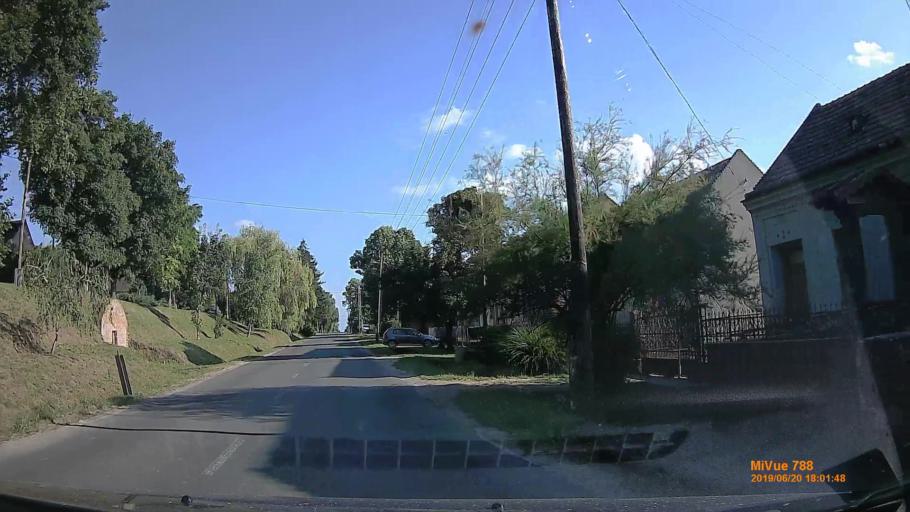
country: HU
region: Baranya
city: Buekkoesd
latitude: 46.0802
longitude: 17.9906
